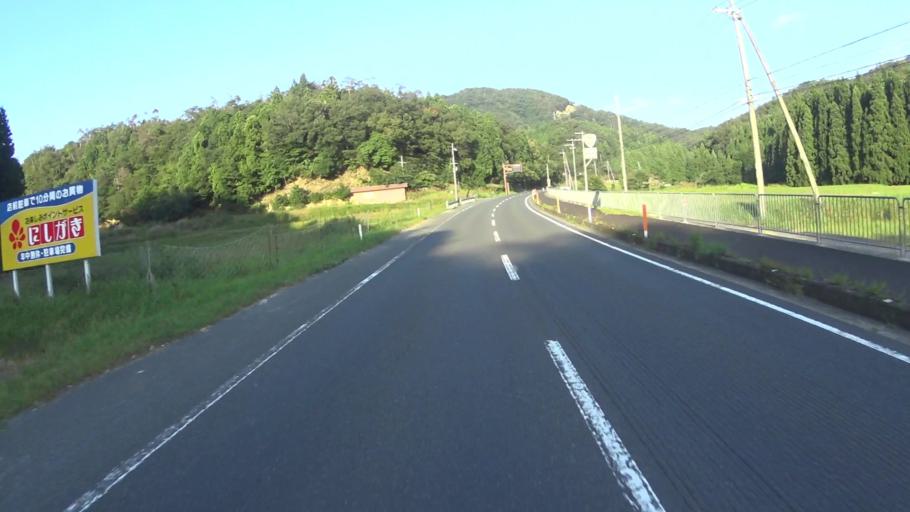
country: JP
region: Hyogo
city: Toyooka
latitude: 35.5757
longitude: 134.9872
